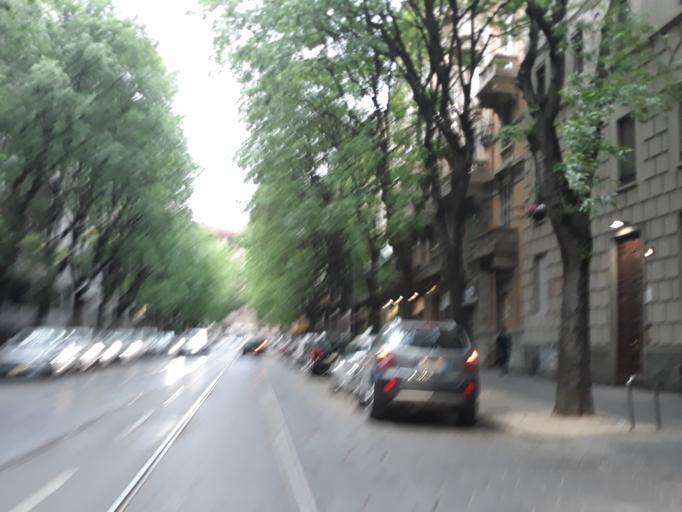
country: IT
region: Lombardy
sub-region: Citta metropolitana di Milano
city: Milano
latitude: 45.4828
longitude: 9.1692
